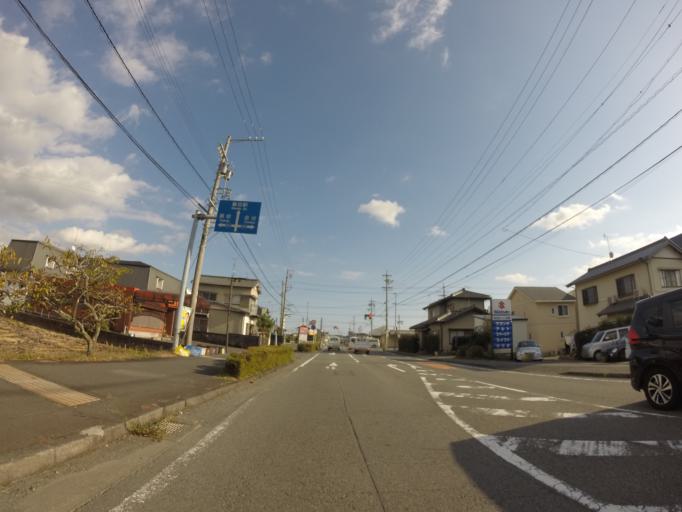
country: JP
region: Shizuoka
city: Kanaya
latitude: 34.8369
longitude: 138.1517
